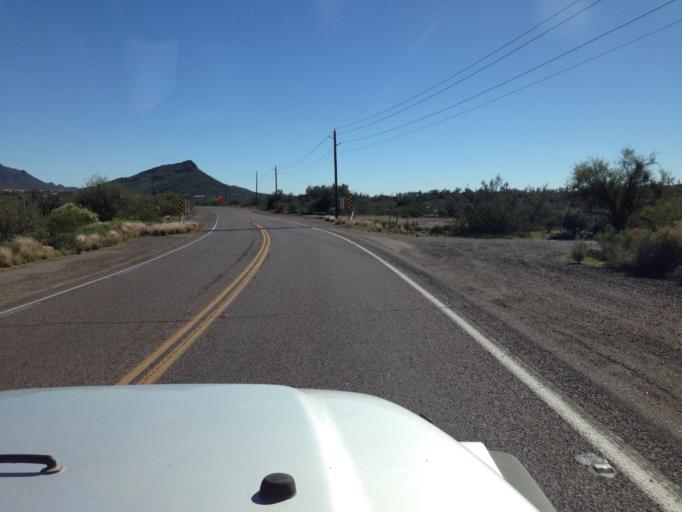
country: US
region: Arizona
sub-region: Maricopa County
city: New River
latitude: 33.9037
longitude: -112.0826
